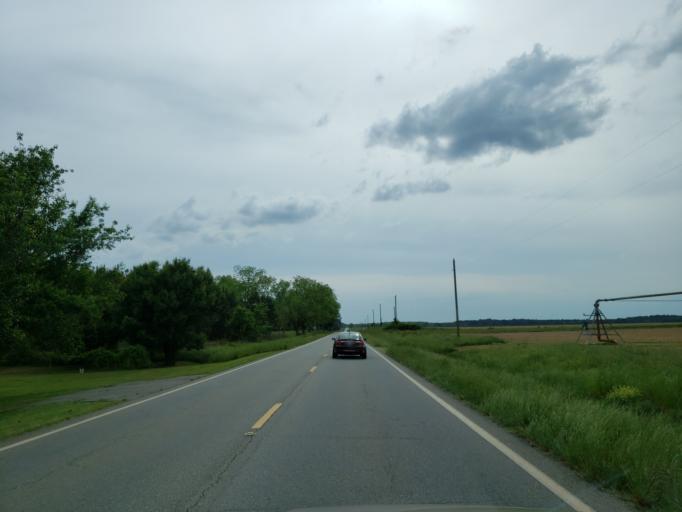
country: US
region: Georgia
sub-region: Houston County
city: Perry
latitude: 32.4296
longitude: -83.8181
